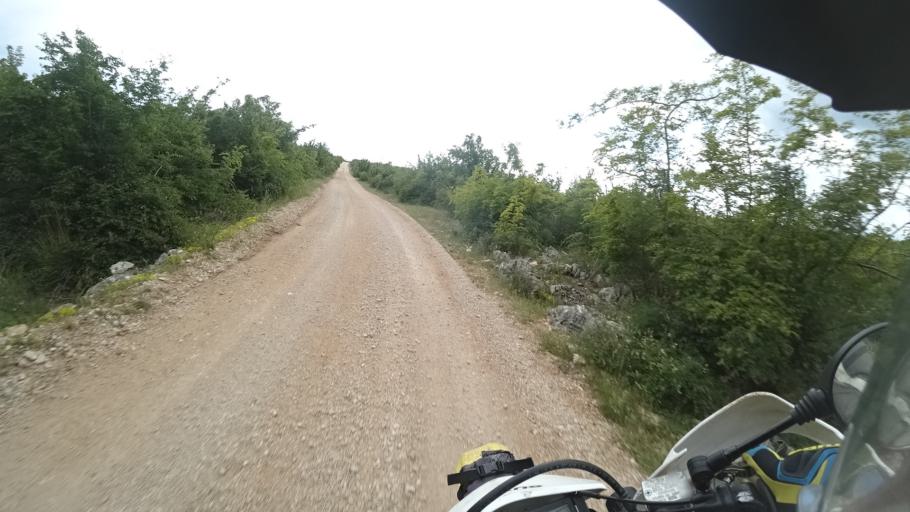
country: HR
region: Sibensko-Kniniska
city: Kistanje
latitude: 44.0998
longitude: 15.9775
